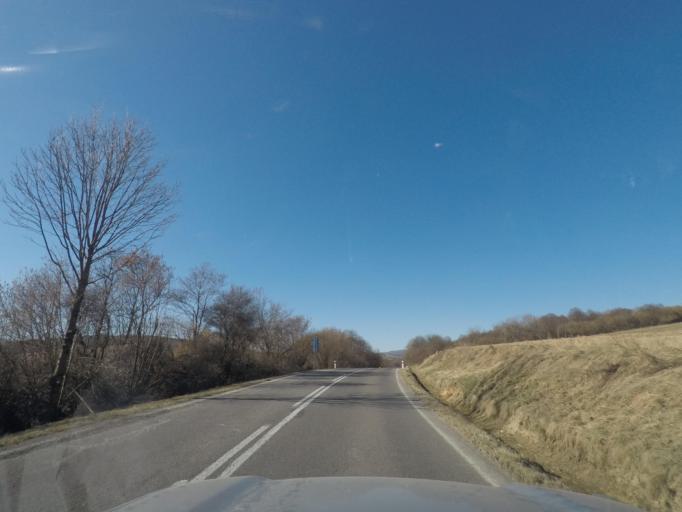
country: UA
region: Zakarpattia
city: Velykyi Bereznyi
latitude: 48.9074
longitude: 22.3747
